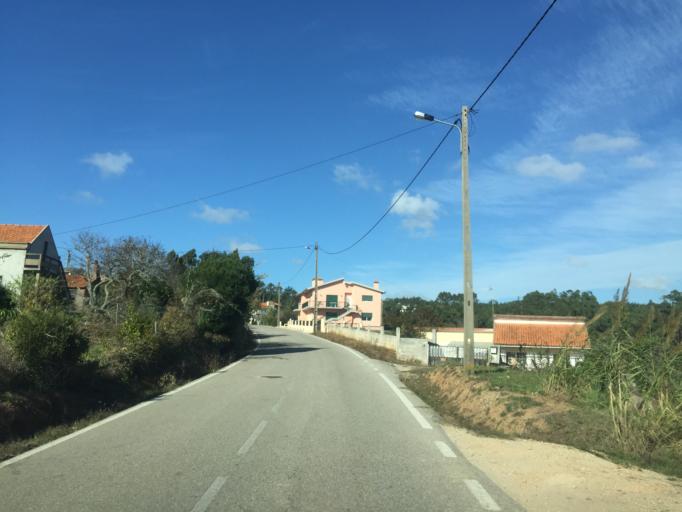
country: PT
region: Coimbra
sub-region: Figueira da Foz
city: Tavarede
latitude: 40.1815
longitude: -8.8376
